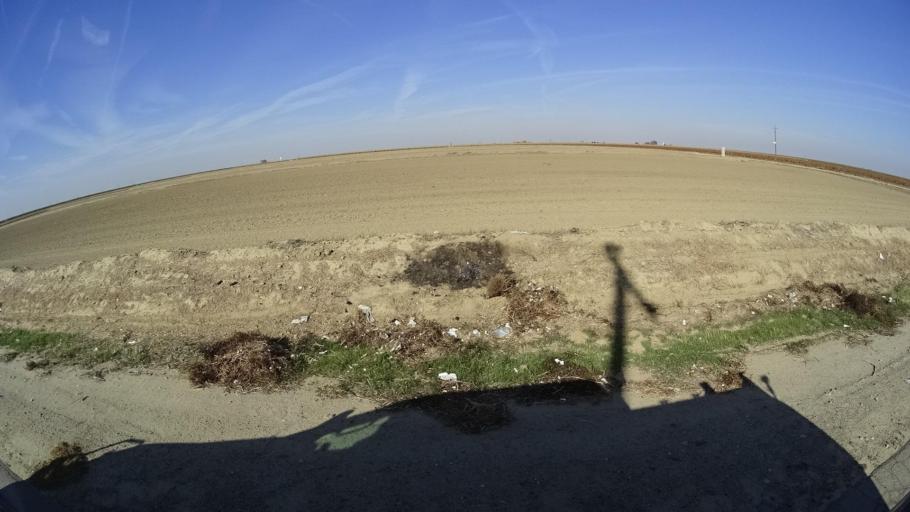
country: US
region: California
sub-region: Kern County
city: Wasco
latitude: 35.7031
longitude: -119.3939
